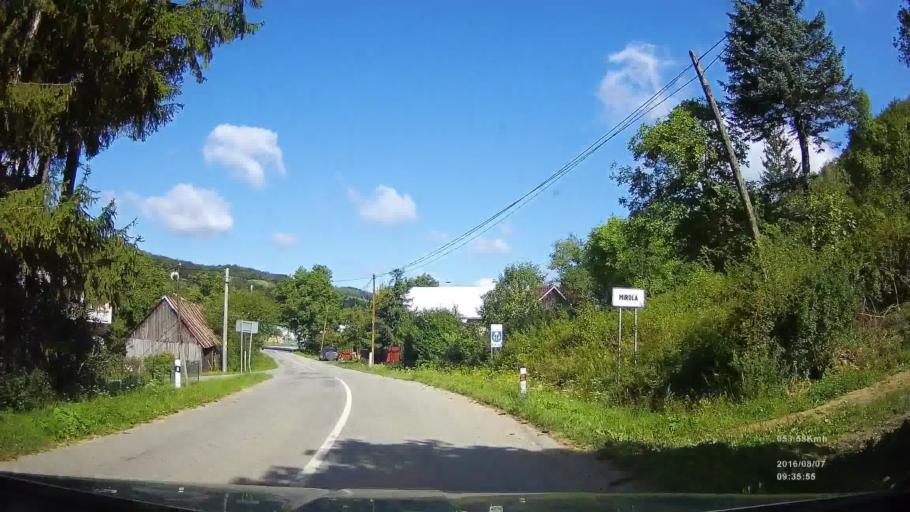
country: PL
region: Subcarpathian Voivodeship
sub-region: Powiat krosnienski
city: Jasliska
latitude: 49.3255
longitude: 21.7354
